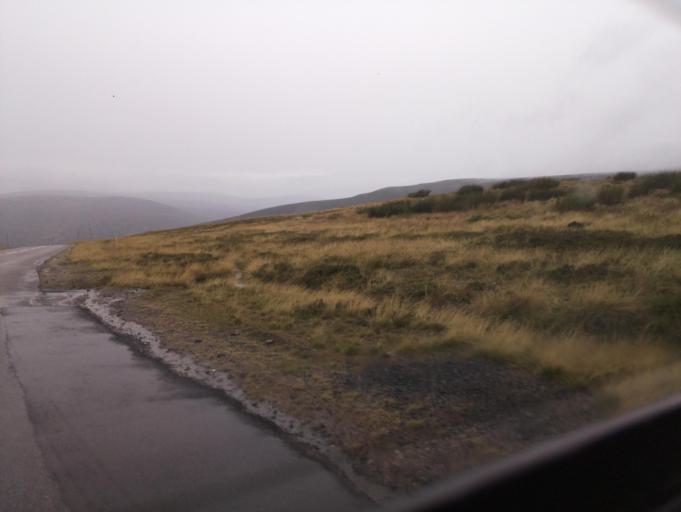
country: GB
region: Scotland
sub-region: Aberdeenshire
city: Ballater
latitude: 57.1904
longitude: -3.2387
